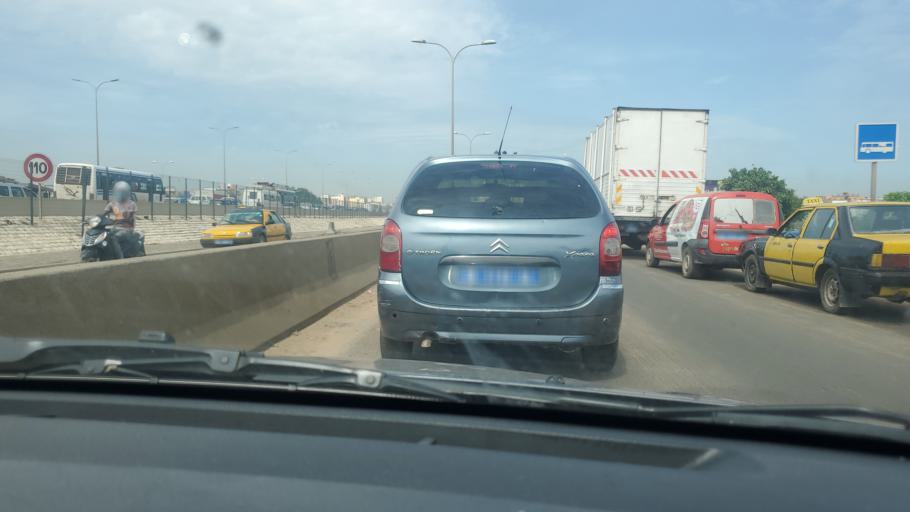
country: SN
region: Dakar
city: Pikine
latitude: 14.7468
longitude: -17.4179
